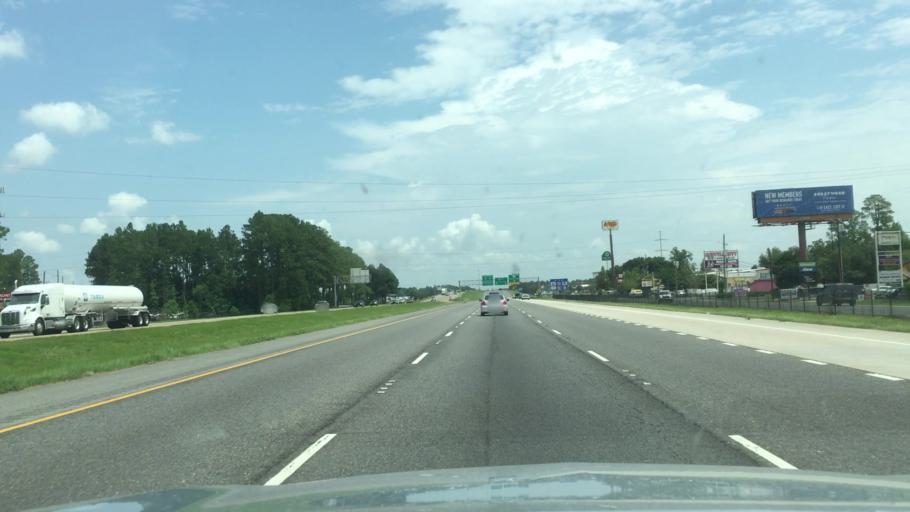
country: US
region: Louisiana
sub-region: Saint Tammany Parish
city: Slidell
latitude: 30.2780
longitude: -89.7518
